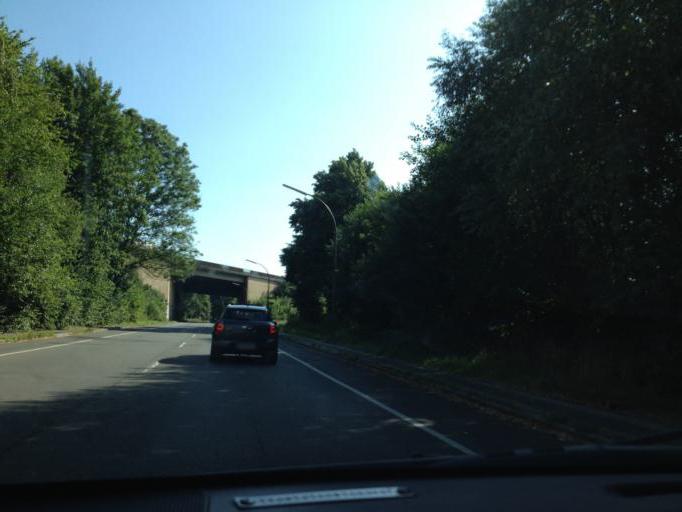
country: DE
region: North Rhine-Westphalia
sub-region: Regierungsbezirk Arnsberg
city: Holzwickede
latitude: 51.5048
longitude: 7.5852
